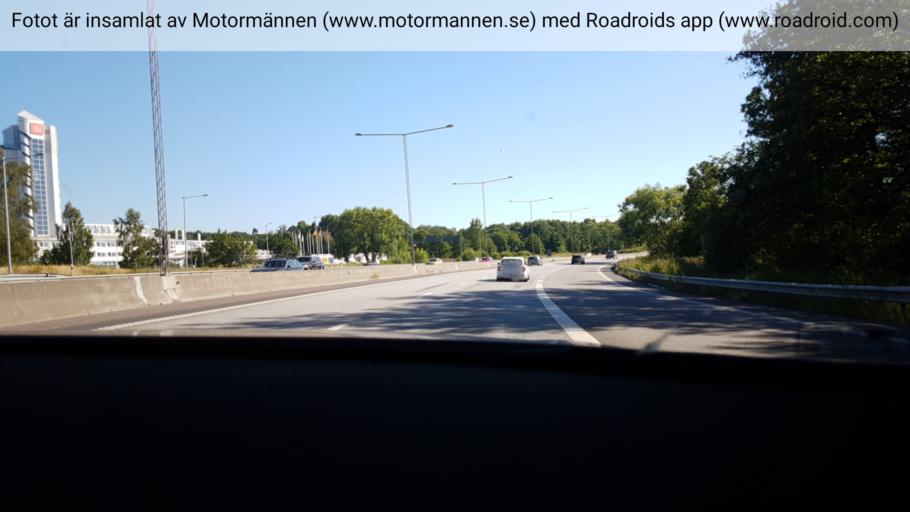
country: SE
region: Joenkoeping
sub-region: Jonkopings Kommun
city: Jonkoping
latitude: 57.7636
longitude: 14.1890
